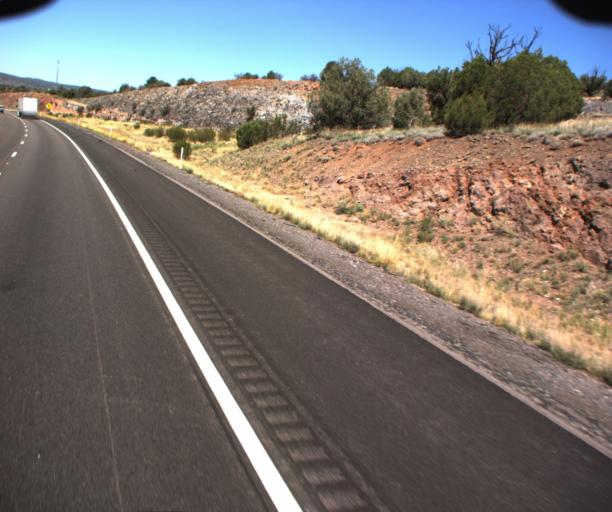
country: US
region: Arizona
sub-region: Mohave County
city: Peach Springs
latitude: 35.1911
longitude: -113.4356
